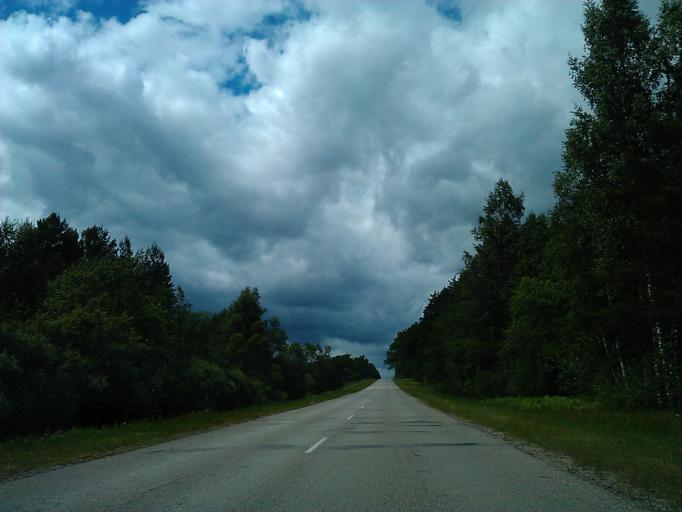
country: LV
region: Talsu Rajons
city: Stende
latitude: 57.0852
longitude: 22.4846
